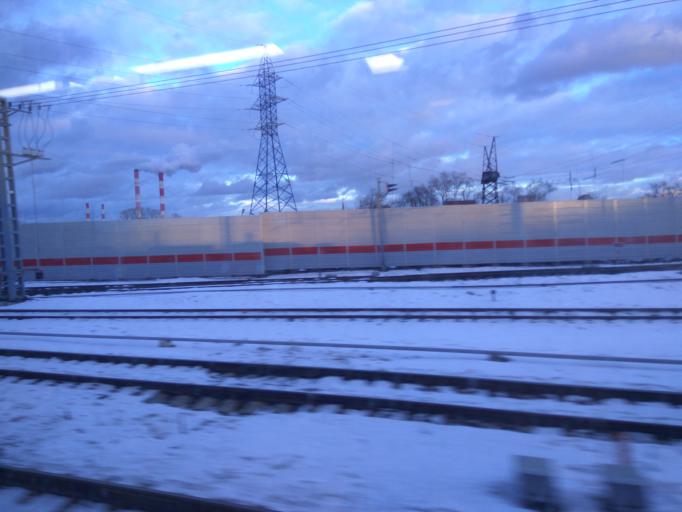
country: RU
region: Moskovskaya
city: Bogorodskoye
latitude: 55.8072
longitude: 37.7461
